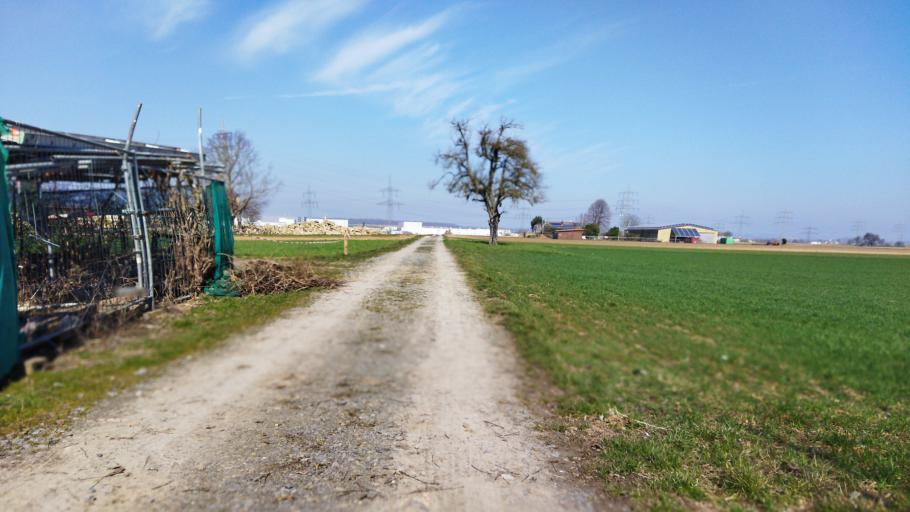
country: DE
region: Baden-Wuerttemberg
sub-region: Regierungsbezirk Stuttgart
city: Untereisesheim
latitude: 49.1670
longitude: 9.1702
